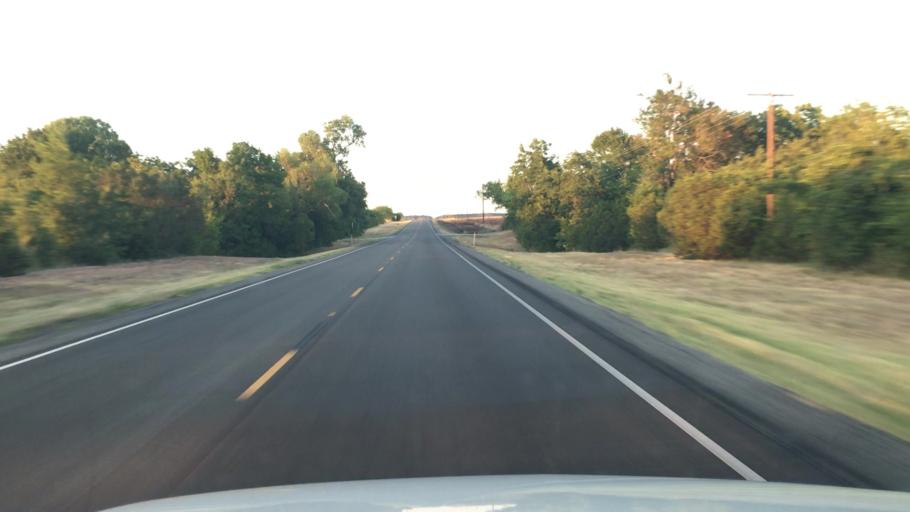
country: US
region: Texas
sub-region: Hamilton County
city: Hico
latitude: 32.0681
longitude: -97.9895
